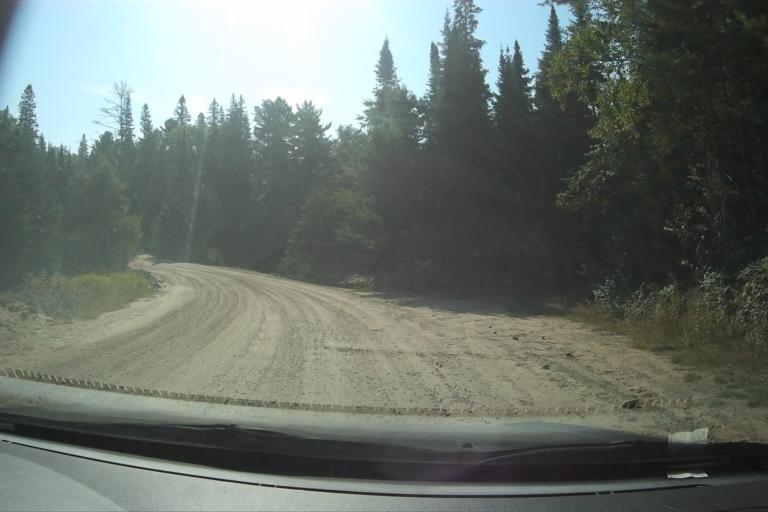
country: CA
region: Ontario
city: Huntsville
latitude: 45.5684
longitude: -78.7102
